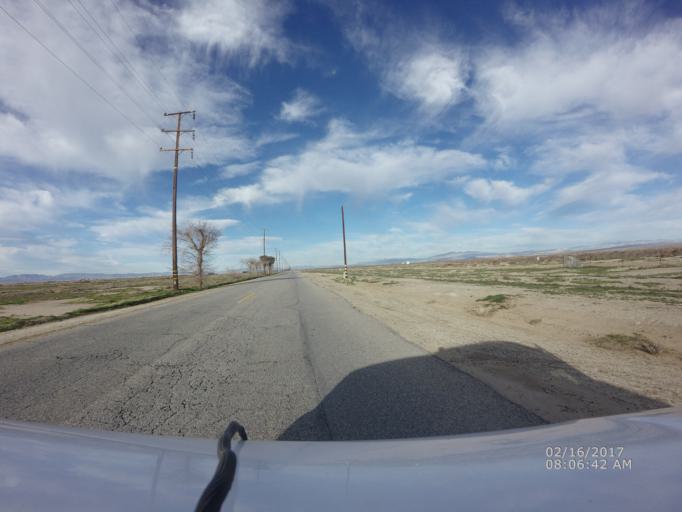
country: US
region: California
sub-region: Kern County
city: Edwards Air Force Base
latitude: 34.7638
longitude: -117.9749
